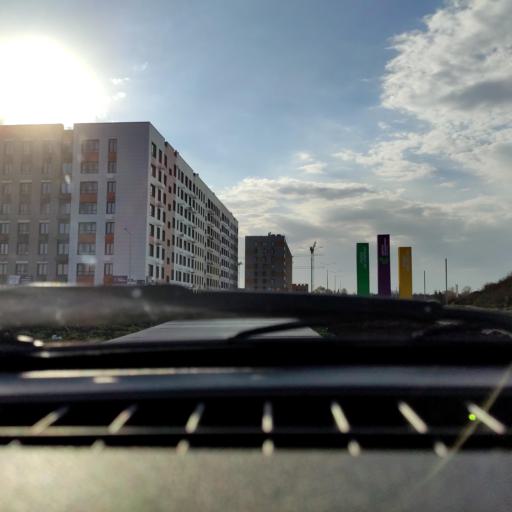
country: RU
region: Bashkortostan
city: Ufa
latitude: 54.6761
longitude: 55.9202
